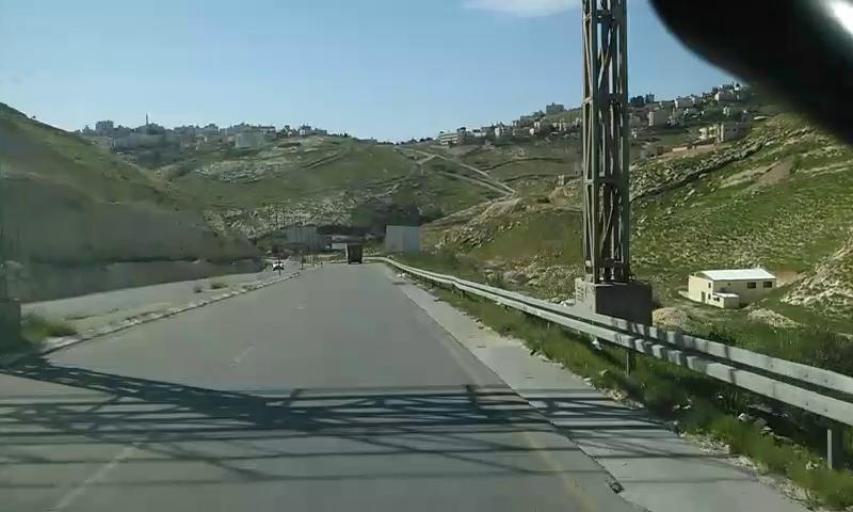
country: PS
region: West Bank
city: Abu Dis
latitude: 31.7480
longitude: 35.2791
